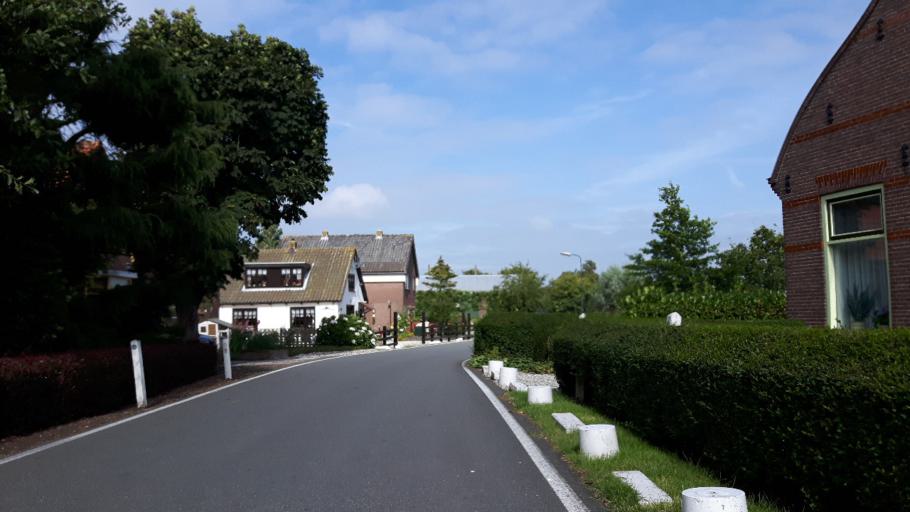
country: NL
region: South Holland
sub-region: Gemeente Nieuwkoop
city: Nieuwkoop
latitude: 52.1236
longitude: 4.7936
